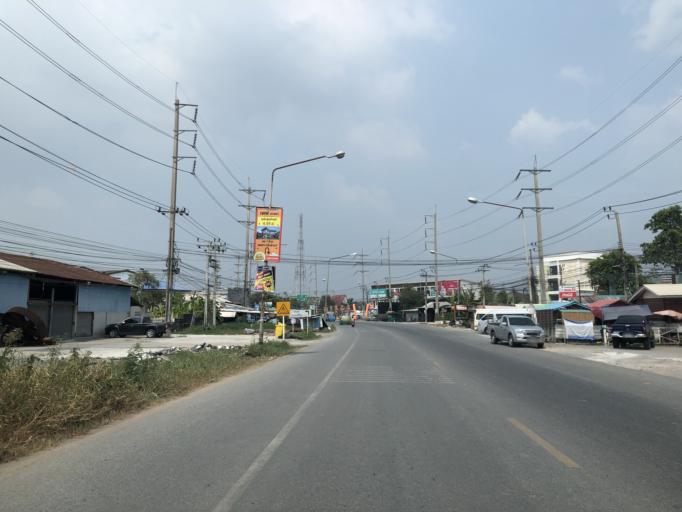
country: TH
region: Samut Prakan
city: Bang Bo
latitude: 13.5676
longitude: 100.8381
